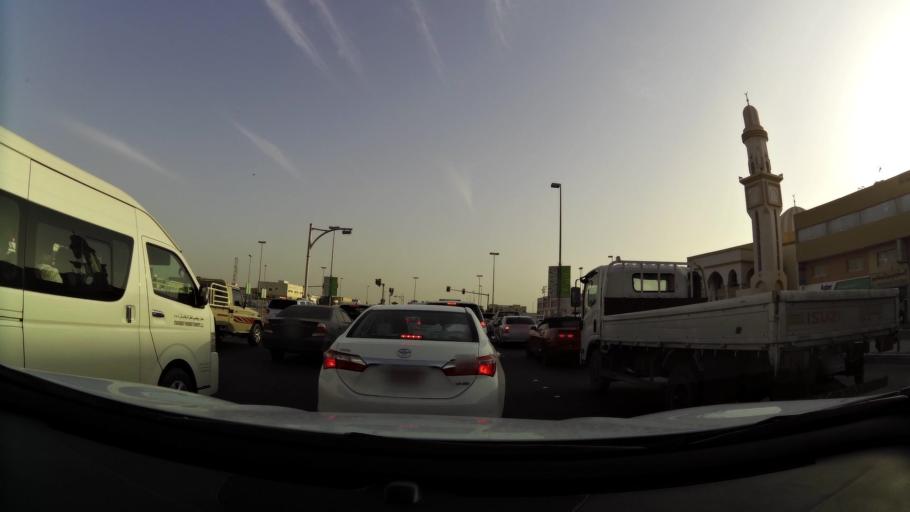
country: AE
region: Abu Dhabi
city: Abu Dhabi
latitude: 24.3742
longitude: 54.5108
